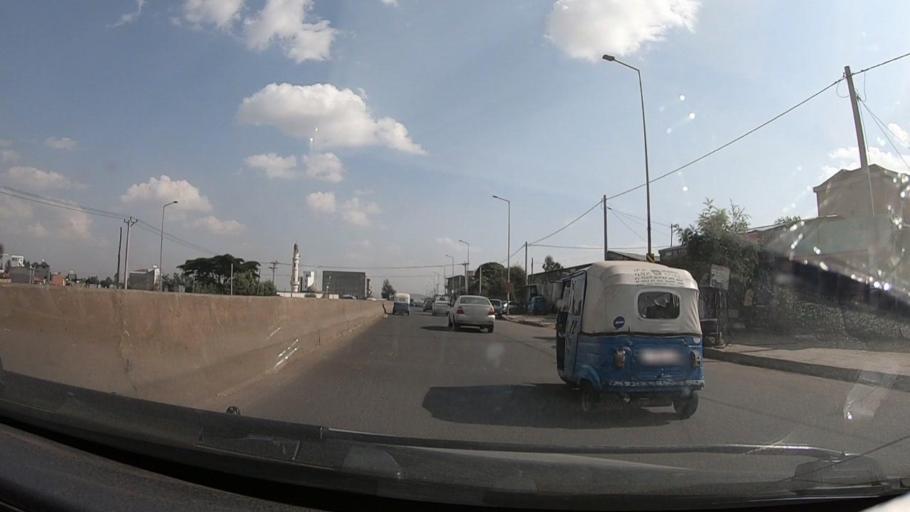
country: ET
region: Adis Abeba
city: Addis Ababa
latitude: 8.9900
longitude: 38.6909
